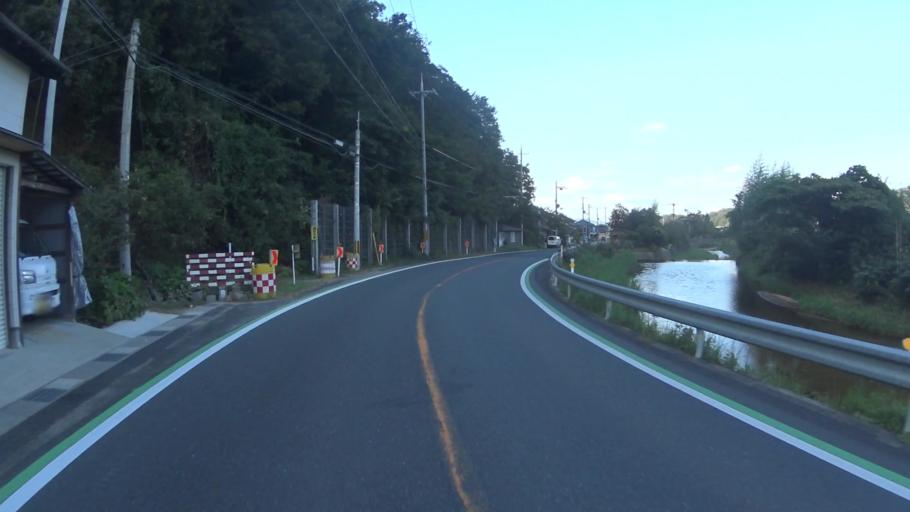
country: JP
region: Kyoto
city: Miyazu
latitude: 35.5854
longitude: 135.0355
